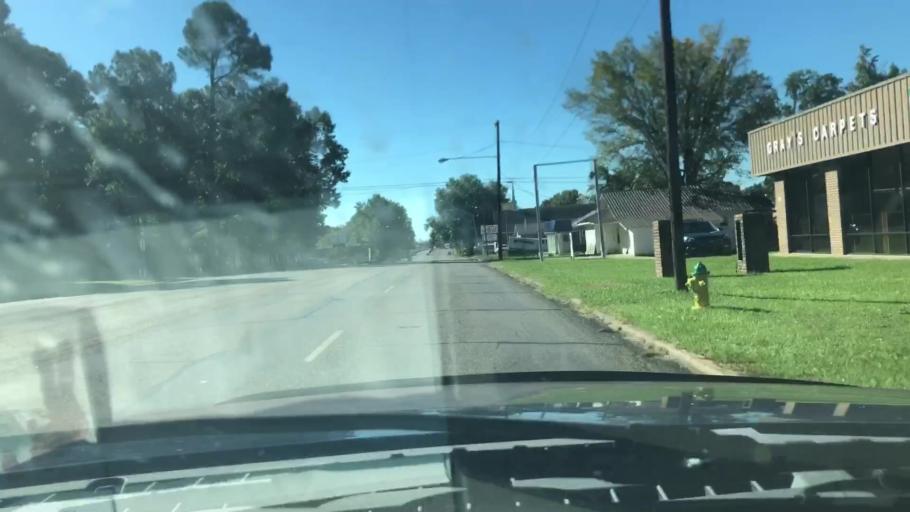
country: US
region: Arkansas
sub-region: Miller County
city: Texarkana
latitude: 33.4438
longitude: -94.0532
